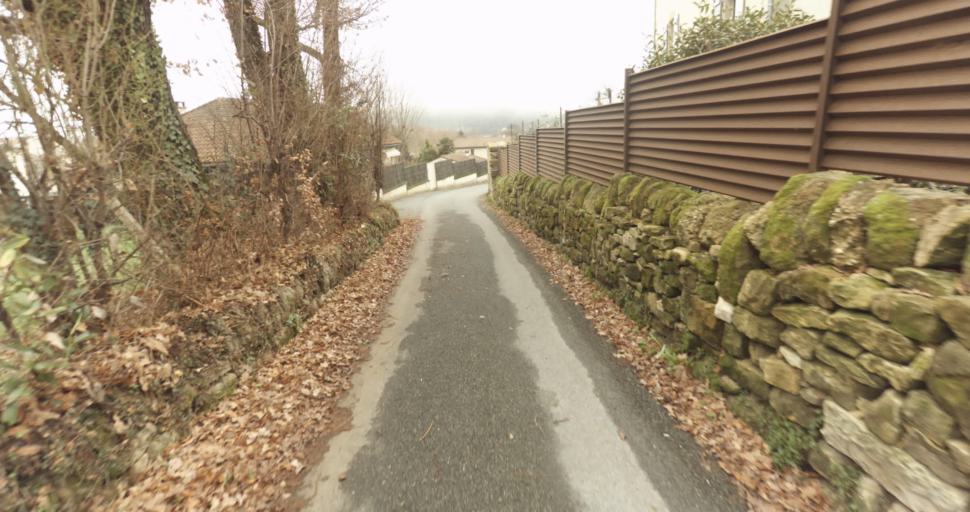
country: FR
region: Midi-Pyrenees
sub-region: Departement du Lot
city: Figeac
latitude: 44.6145
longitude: 2.0402
